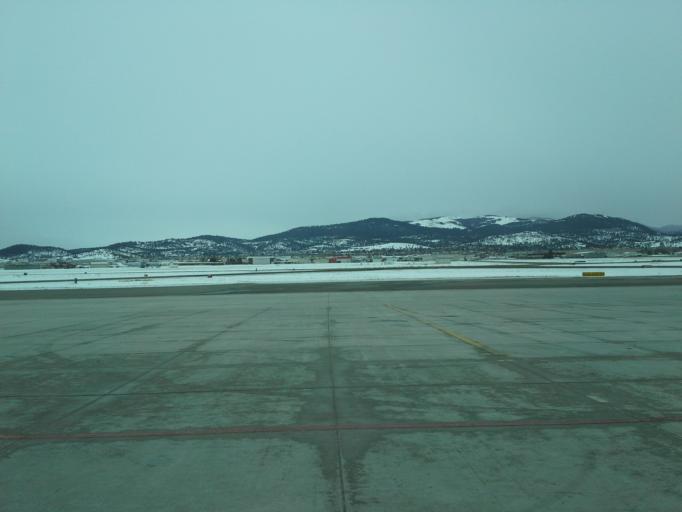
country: US
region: Montana
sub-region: Lewis and Clark County
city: Helena
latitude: 46.6102
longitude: -111.9893
